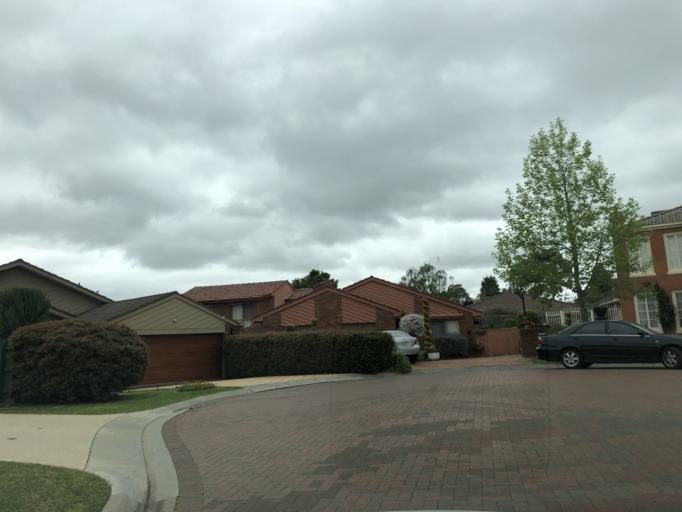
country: AU
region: Victoria
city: Burwood East
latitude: -37.8603
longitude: 145.1628
